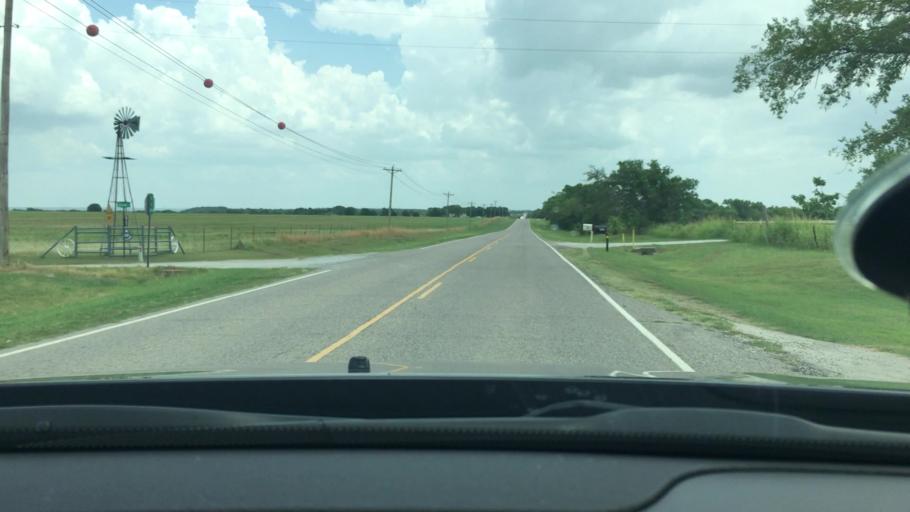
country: US
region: Oklahoma
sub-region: Love County
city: Marietta
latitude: 33.9403
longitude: -97.0571
